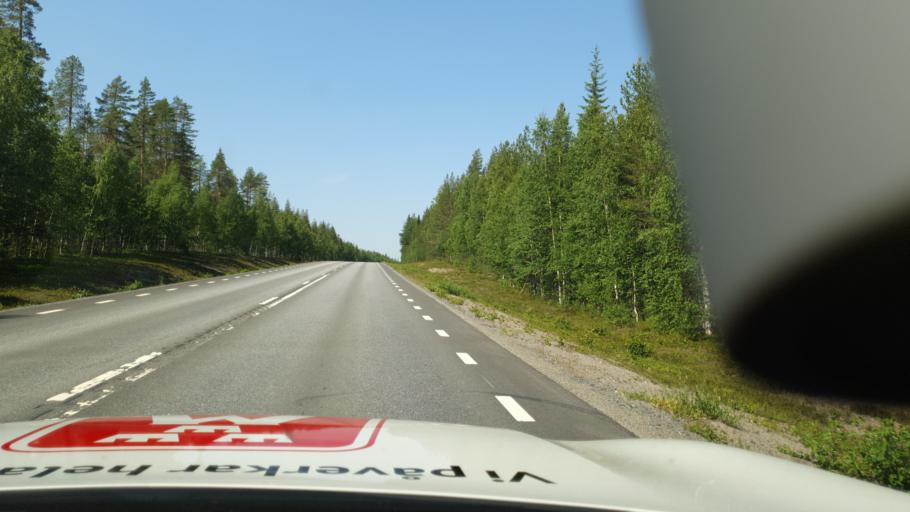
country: SE
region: Vaesterbotten
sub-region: Norsjo Kommun
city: Norsjoe
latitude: 64.9690
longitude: 19.7730
